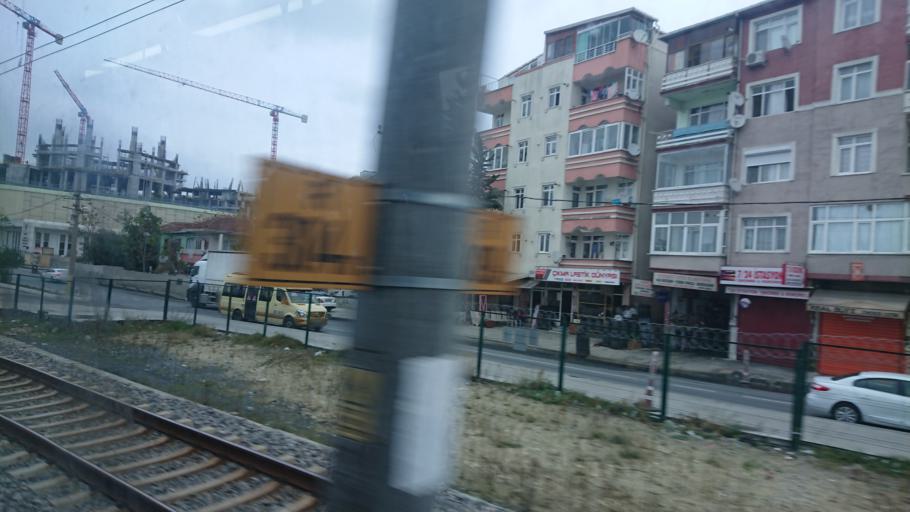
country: TR
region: Istanbul
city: Mahmutbey
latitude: 41.0111
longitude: 28.7726
